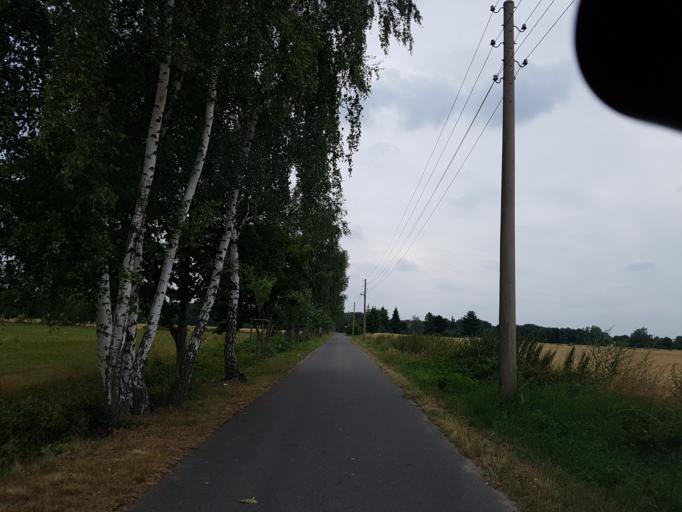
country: DE
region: Brandenburg
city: Sallgast
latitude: 51.5838
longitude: 13.8546
